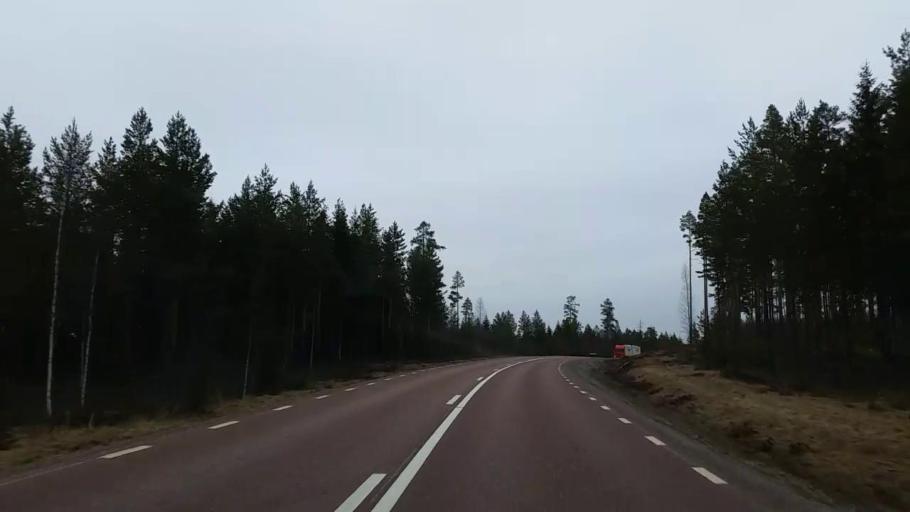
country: SE
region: Gaevleborg
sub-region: Ovanakers Kommun
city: Edsbyn
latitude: 61.2783
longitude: 15.8969
